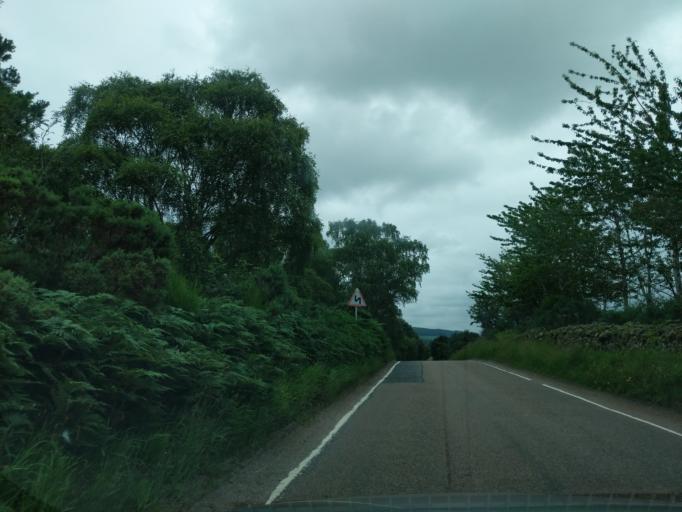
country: GB
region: Scotland
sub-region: Moray
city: Kinloss
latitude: 57.5747
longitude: -3.5459
